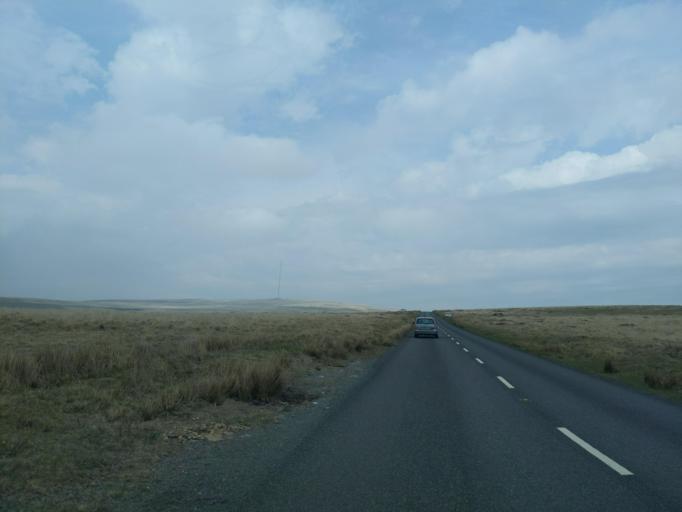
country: GB
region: England
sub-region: Devon
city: Yelverton
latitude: 50.5269
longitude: -4.0206
